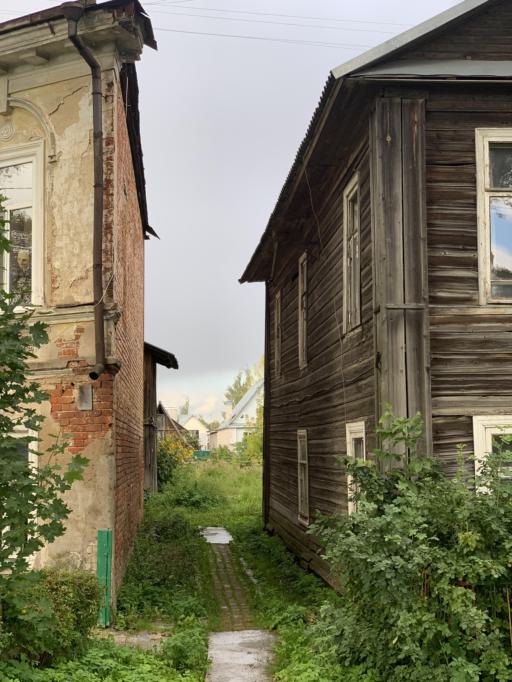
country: RU
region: Tverskaya
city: Vyshniy Volochek
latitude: 57.5864
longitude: 34.5509
